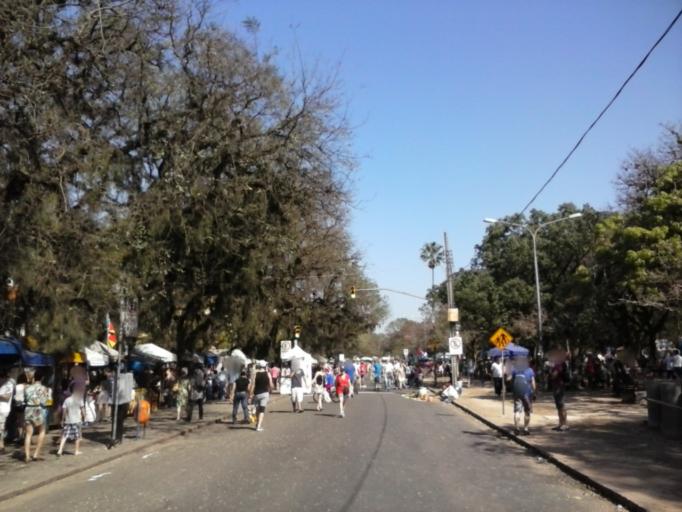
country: BR
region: Rio Grande do Sul
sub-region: Porto Alegre
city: Porto Alegre
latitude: -30.0374
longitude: -51.2123
